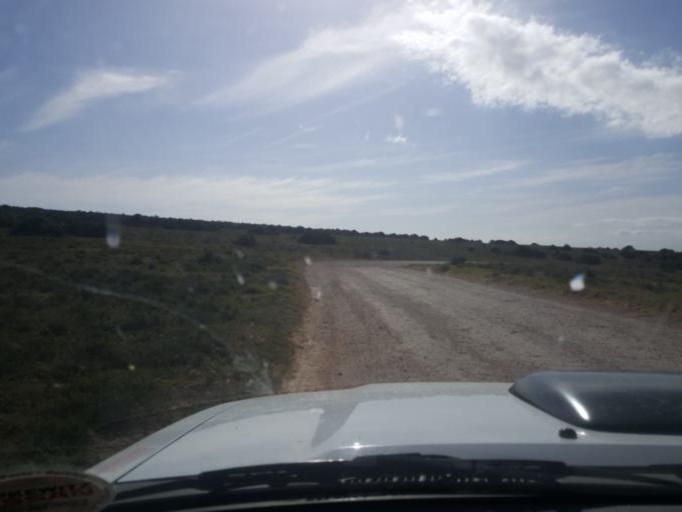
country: ZA
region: Eastern Cape
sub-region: Cacadu District Municipality
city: Kirkwood
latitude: -33.4462
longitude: 25.7974
